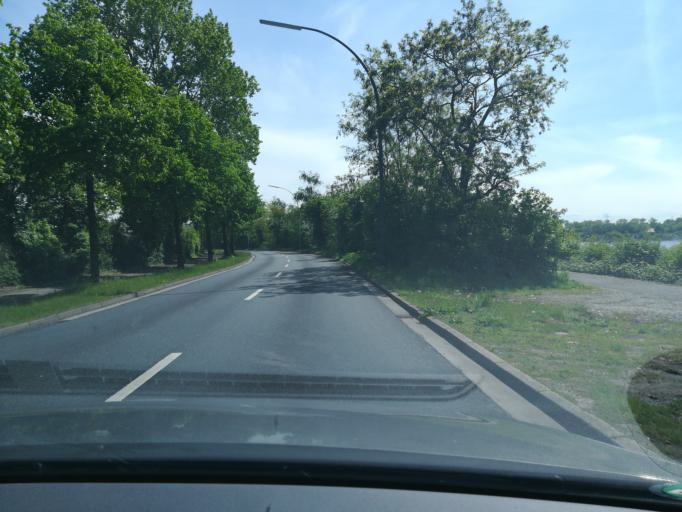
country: DE
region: Hamburg
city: Altona
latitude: 53.5029
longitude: 9.9452
